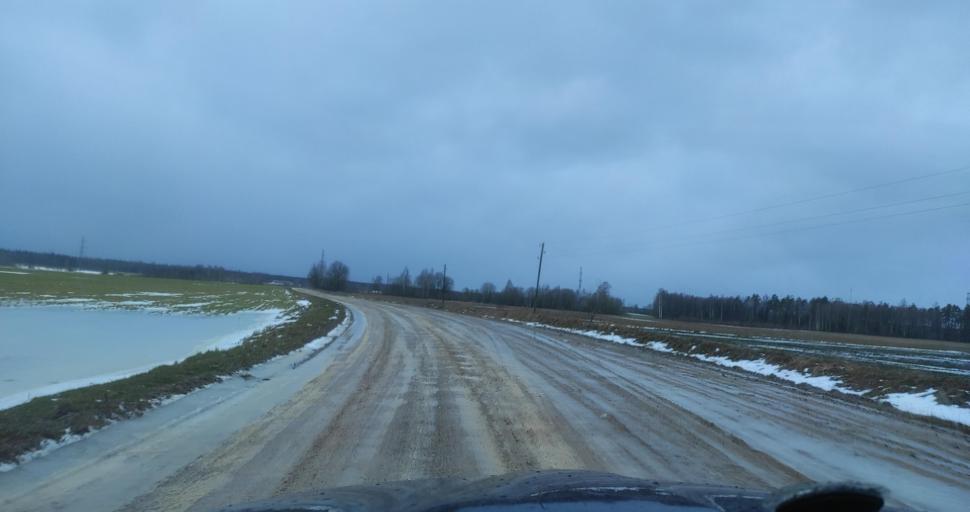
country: LV
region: Dundaga
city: Dundaga
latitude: 57.4663
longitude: 22.0312
